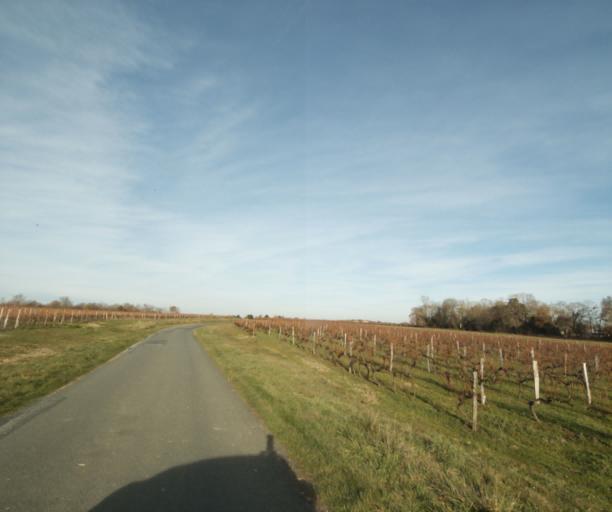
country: FR
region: Poitou-Charentes
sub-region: Departement de la Charente-Maritime
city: Chaniers
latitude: 45.7481
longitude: -0.5217
